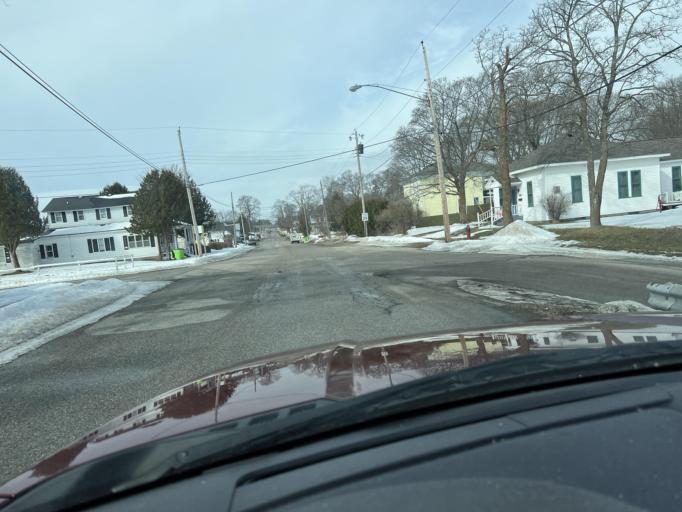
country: US
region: Michigan
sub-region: Mackinac County
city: Saint Ignace
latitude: 45.8674
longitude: -84.7281
